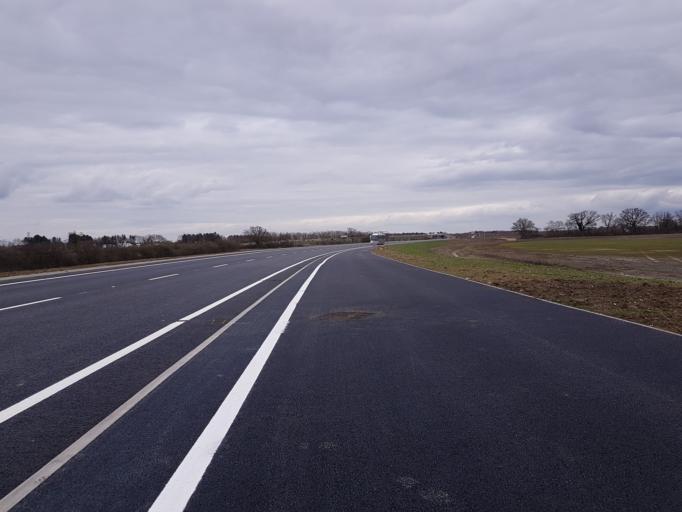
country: GB
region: England
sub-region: Cambridgeshire
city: Girton
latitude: 52.2387
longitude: 0.0537
